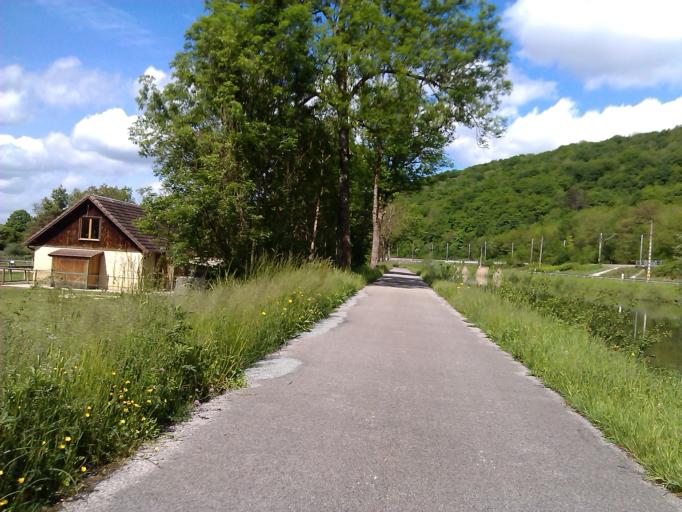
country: FR
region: Franche-Comte
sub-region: Departement du Doubs
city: Nancray
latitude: 47.2900
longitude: 6.1846
